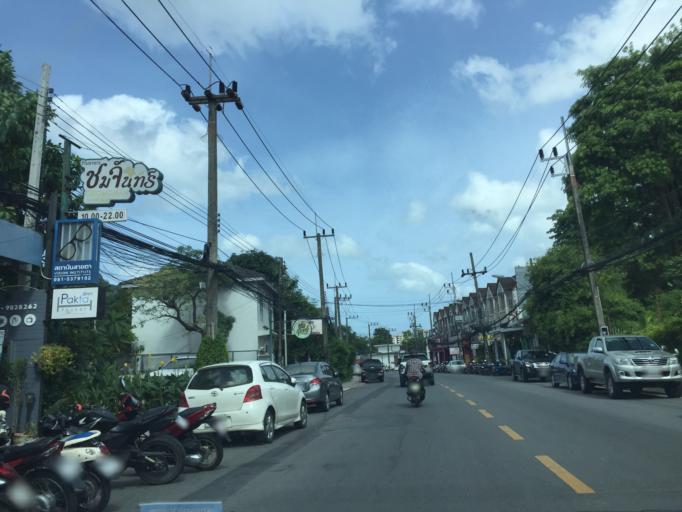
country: TH
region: Phuket
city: Wichit
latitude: 7.9005
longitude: 98.3818
